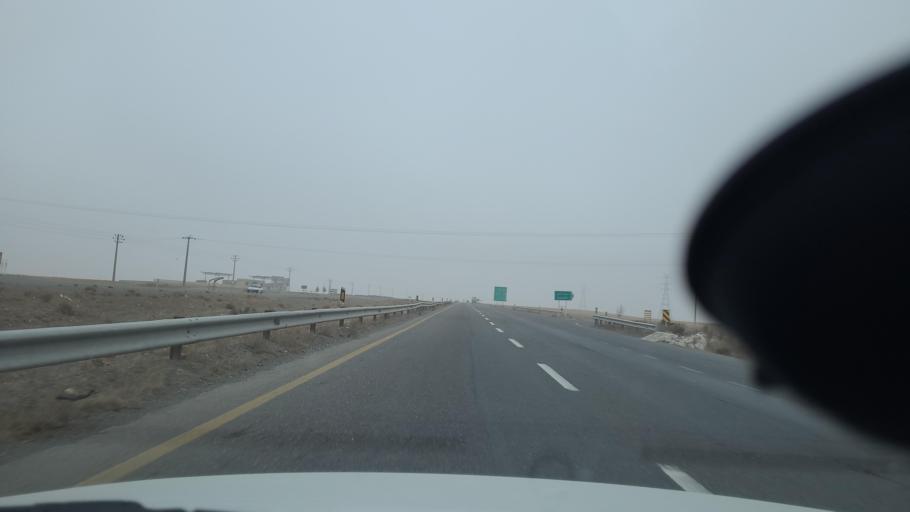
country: IR
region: Razavi Khorasan
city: Fariman
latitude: 35.8744
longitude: 59.7610
